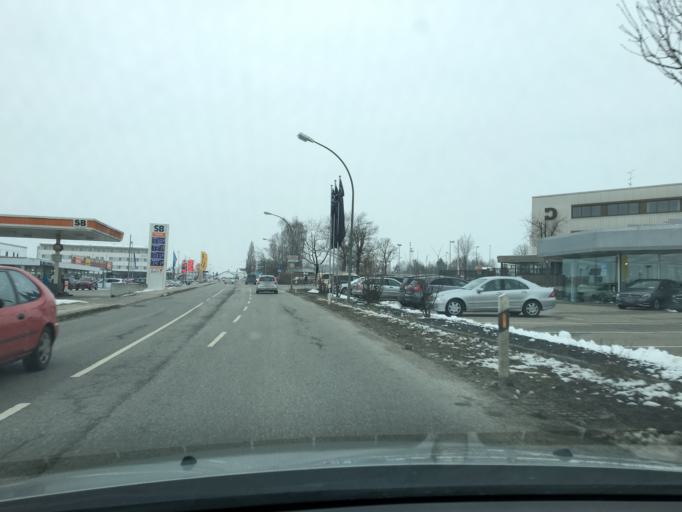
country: DE
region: Bavaria
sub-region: Lower Bavaria
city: Vilsbiburg
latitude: 48.4514
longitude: 12.3435
